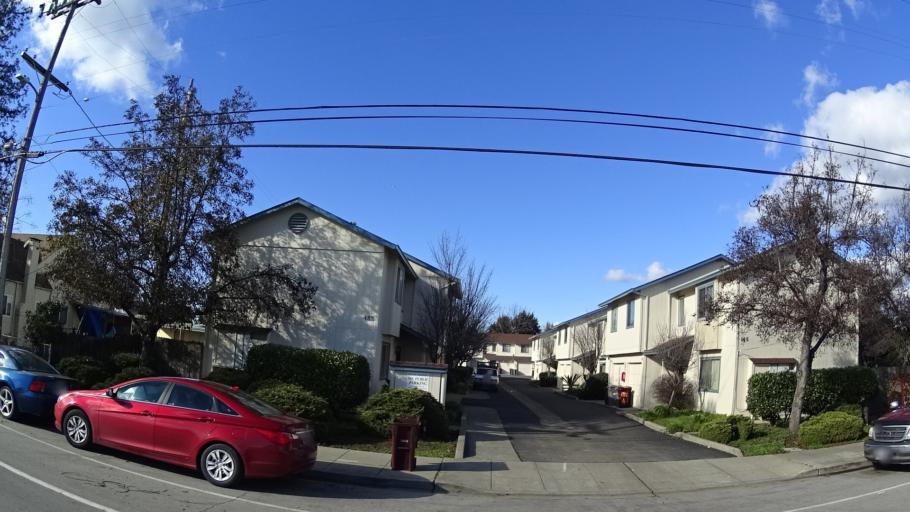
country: US
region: California
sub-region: Alameda County
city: Cherryland
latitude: 37.6747
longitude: -122.0963
